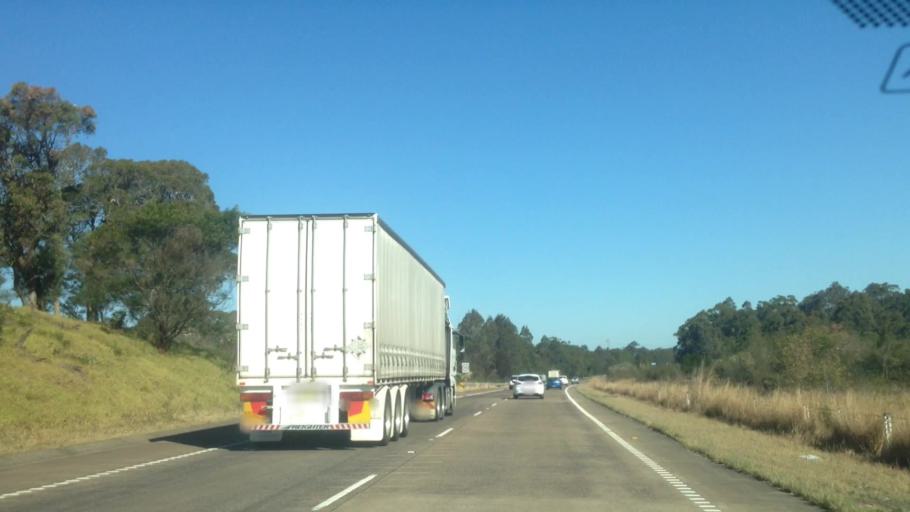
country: AU
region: New South Wales
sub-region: Wyong Shire
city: Charmhaven
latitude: -33.1823
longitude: 151.4679
